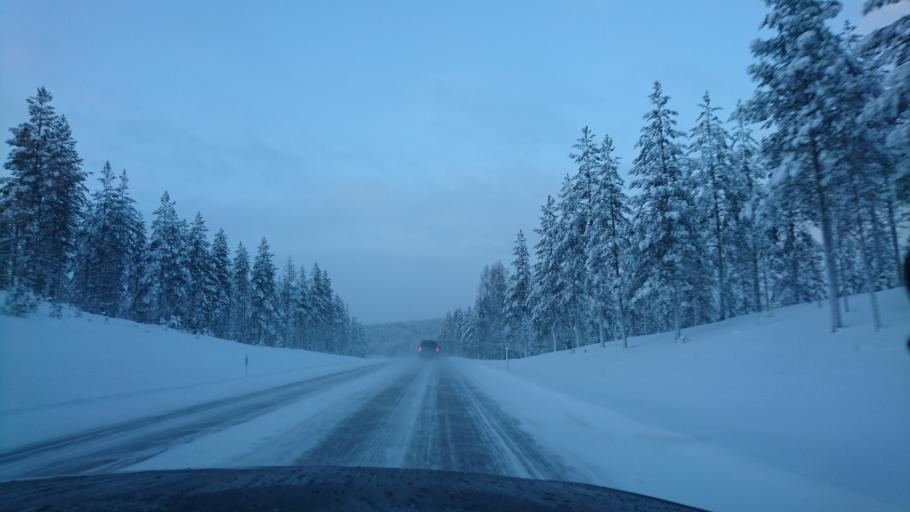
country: FI
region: Northern Ostrobothnia
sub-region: Koillismaa
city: Taivalkoski
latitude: 65.4684
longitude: 27.7045
